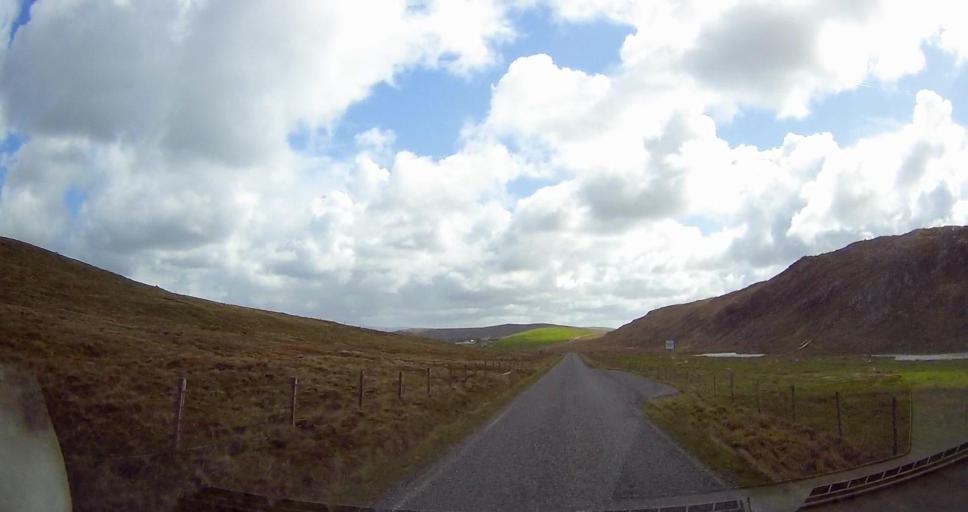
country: GB
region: Scotland
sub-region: Shetland Islands
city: Lerwick
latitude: 60.5558
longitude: -1.3391
